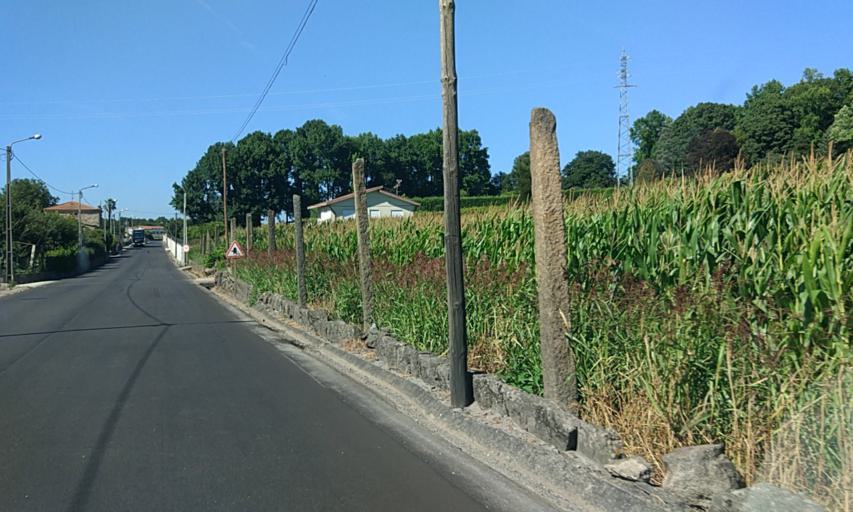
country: PT
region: Porto
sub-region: Trofa
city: Sao Romao do Coronado
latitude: 41.2930
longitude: -8.5996
